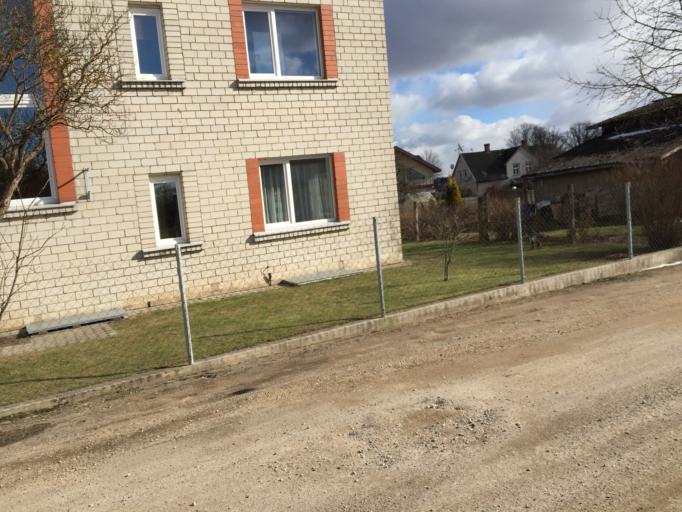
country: LV
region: Valmieras Rajons
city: Valmiera
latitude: 57.5452
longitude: 25.4294
